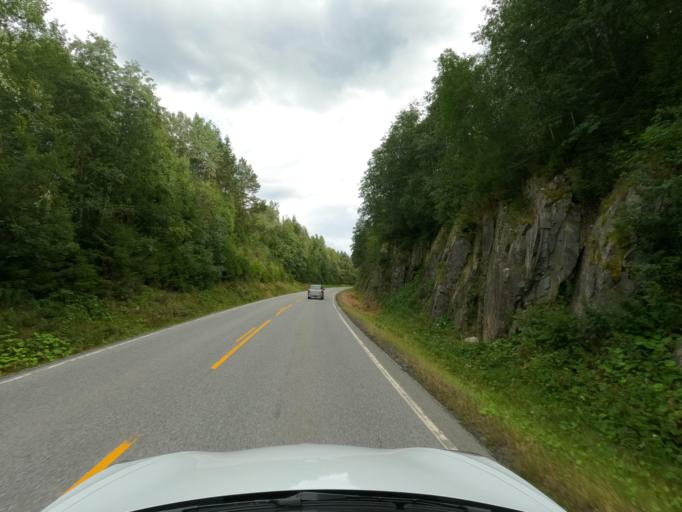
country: NO
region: Telemark
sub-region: Hjartdal
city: Sauland
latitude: 59.8269
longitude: 8.9793
